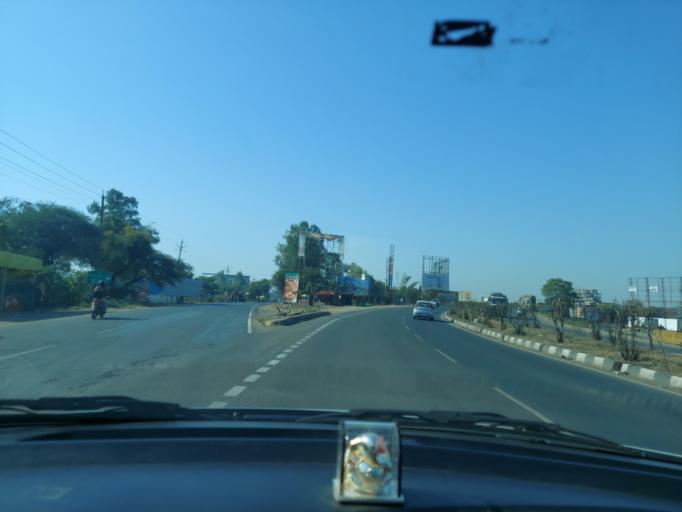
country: IN
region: Madhya Pradesh
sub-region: Indore
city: Pithampur
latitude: 22.6109
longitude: 75.7964
